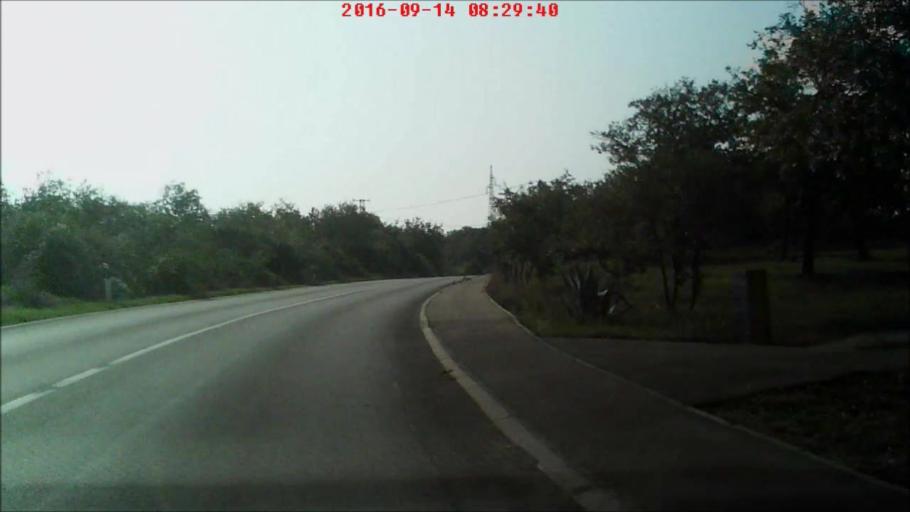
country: HR
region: Zadarska
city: Zadar
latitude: 44.1788
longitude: 15.2859
